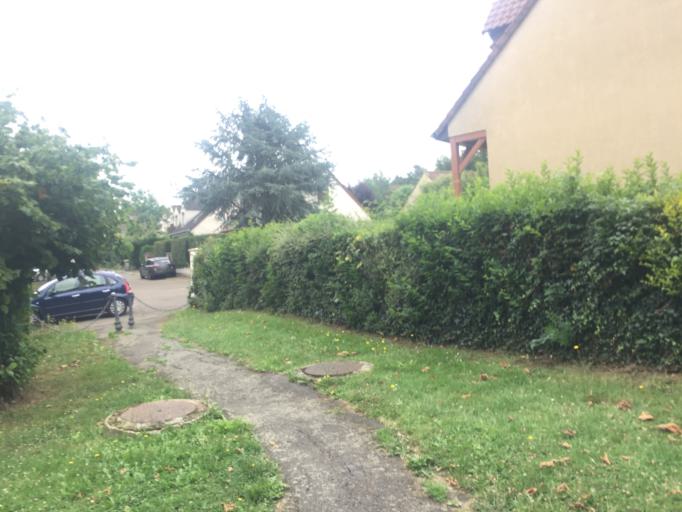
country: FR
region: Ile-de-France
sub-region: Departement des Yvelines
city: Villepreux
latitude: 48.8155
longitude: 2.0006
